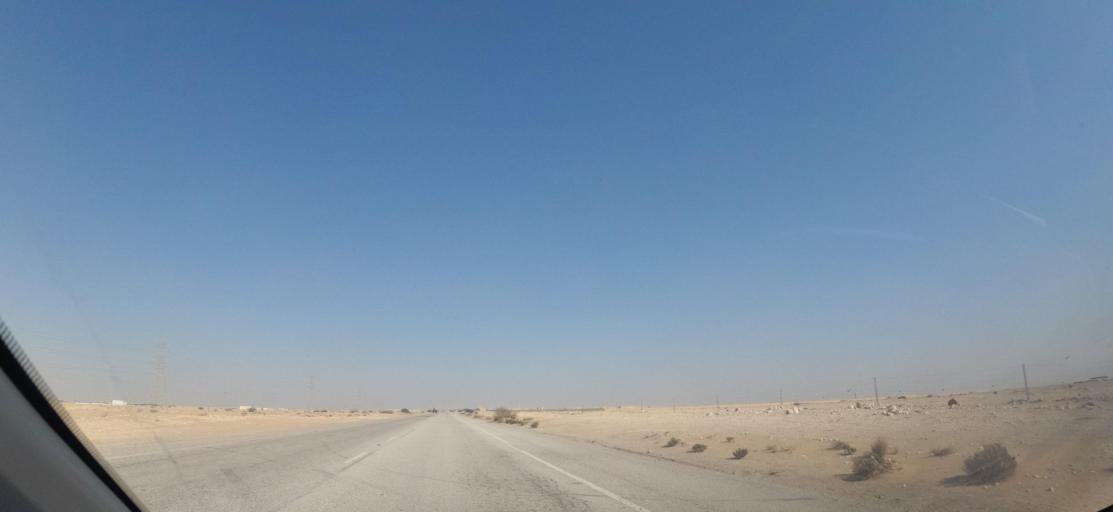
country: QA
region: Baladiyat ar Rayyan
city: Dukhan
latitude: 25.4804
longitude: 50.9590
